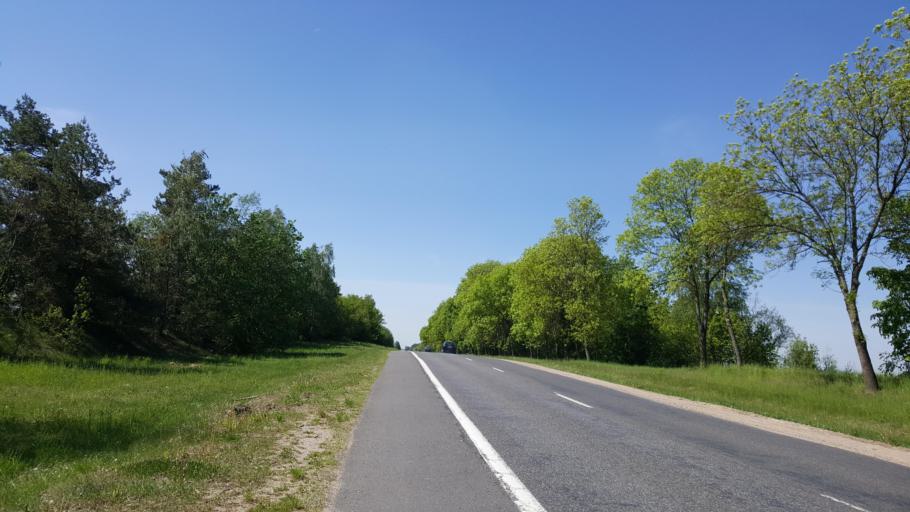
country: BY
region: Brest
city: Kamyanyets
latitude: 52.3853
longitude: 23.8145
